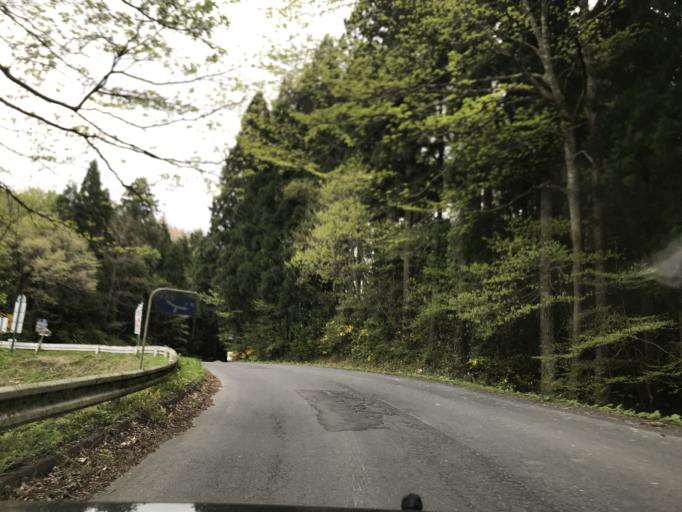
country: JP
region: Iwate
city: Ichinoseki
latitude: 38.8285
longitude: 141.3644
